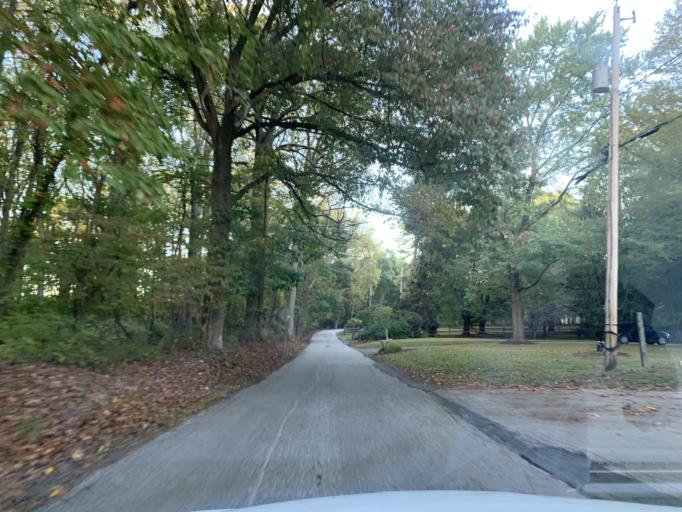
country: US
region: Maryland
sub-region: Harford County
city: Fallston
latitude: 39.4994
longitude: -76.4364
